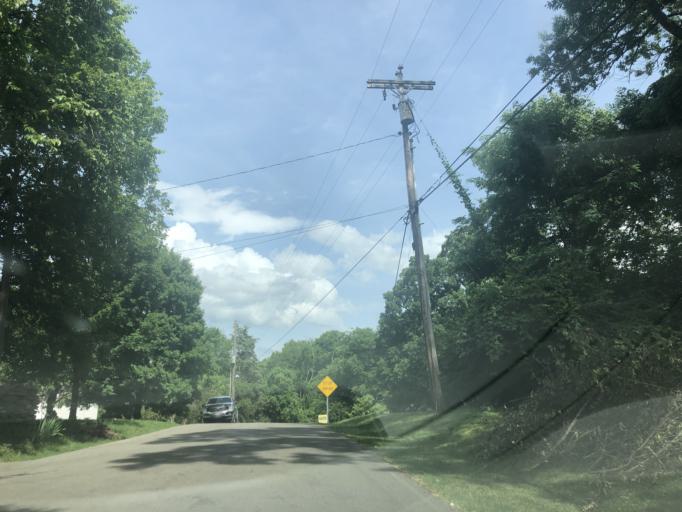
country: US
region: Tennessee
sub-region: Davidson County
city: Oak Hill
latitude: 36.0862
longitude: -86.8007
